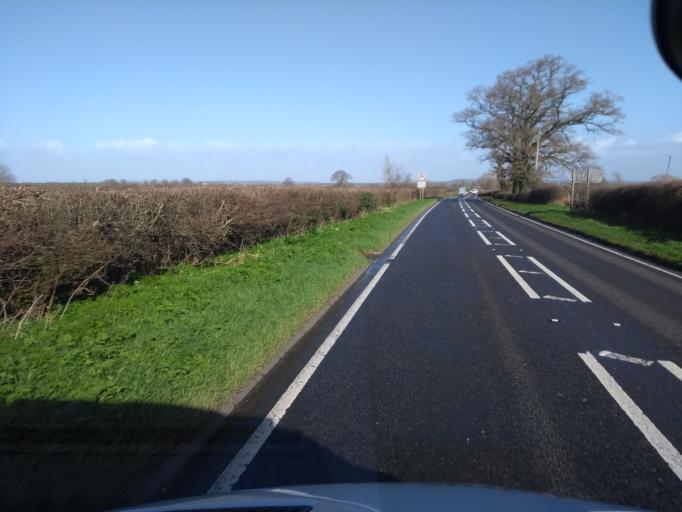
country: GB
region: England
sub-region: Somerset
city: Ilchester
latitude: 50.9784
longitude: -2.6734
